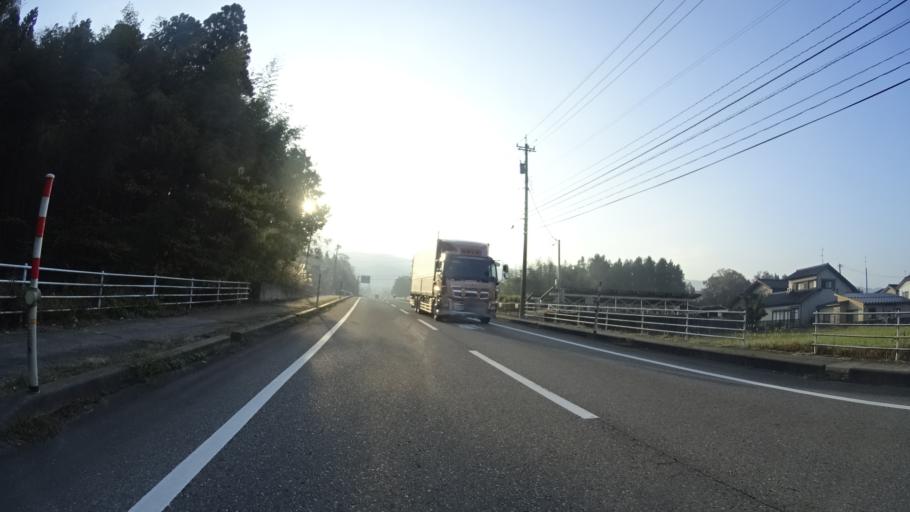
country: JP
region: Ishikawa
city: Nanao
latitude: 37.0278
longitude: 136.9741
